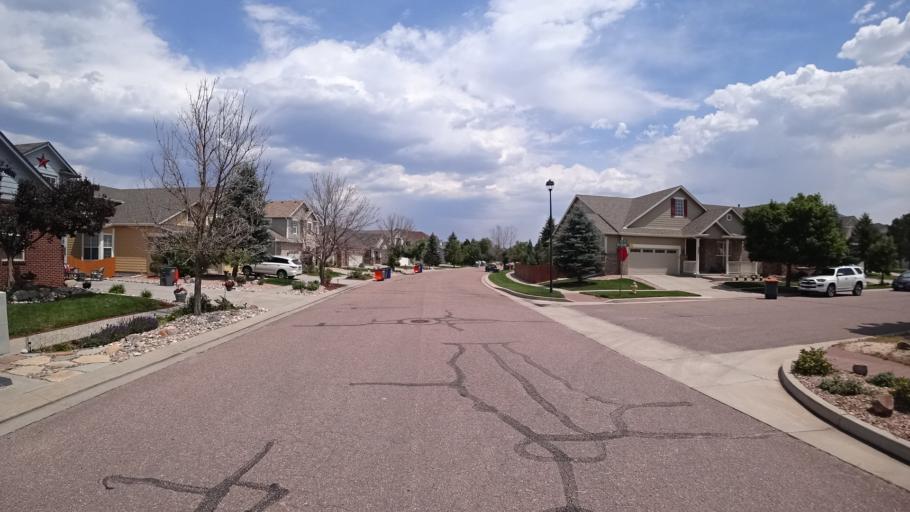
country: US
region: Colorado
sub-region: El Paso County
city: Black Forest
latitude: 38.9620
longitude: -104.7616
